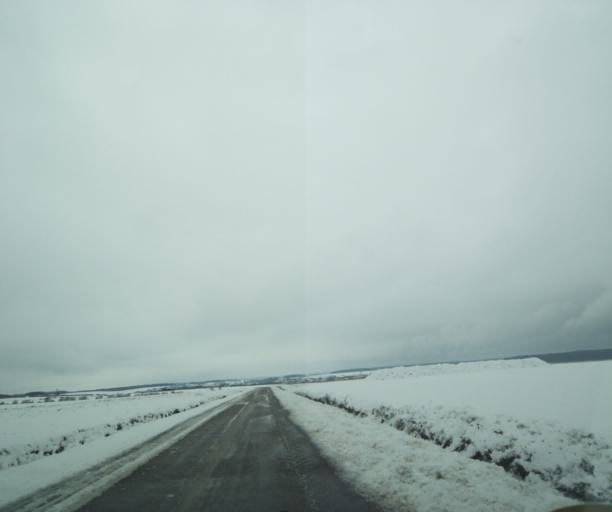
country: FR
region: Champagne-Ardenne
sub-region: Departement de la Haute-Marne
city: Laneuville-a-Remy
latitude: 48.3972
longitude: 4.8635
